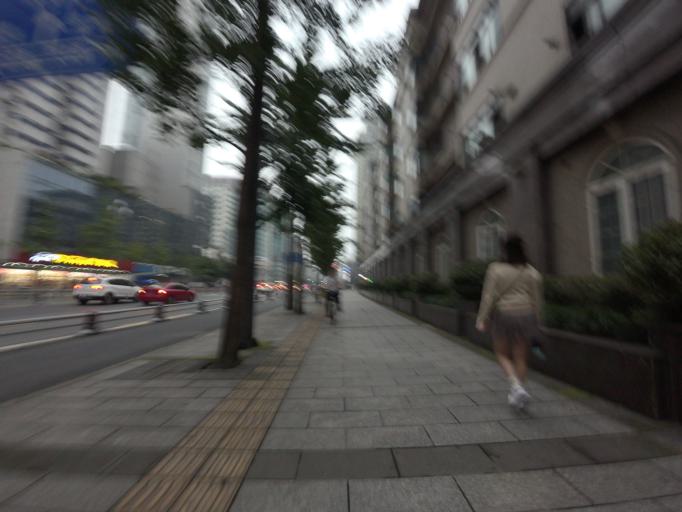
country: CN
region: Sichuan
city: Chengdu
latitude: 30.6741
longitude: 104.0647
